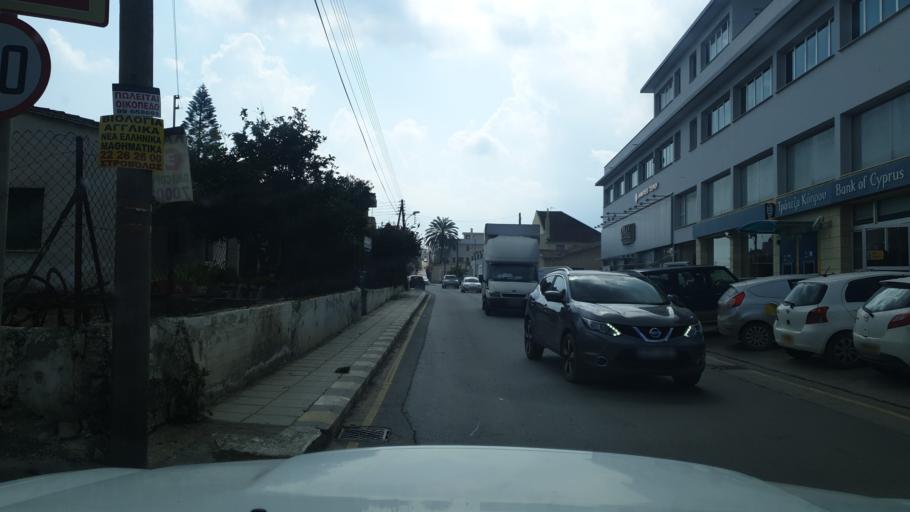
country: CY
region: Lefkosia
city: Tseri
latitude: 35.0761
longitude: 33.3244
